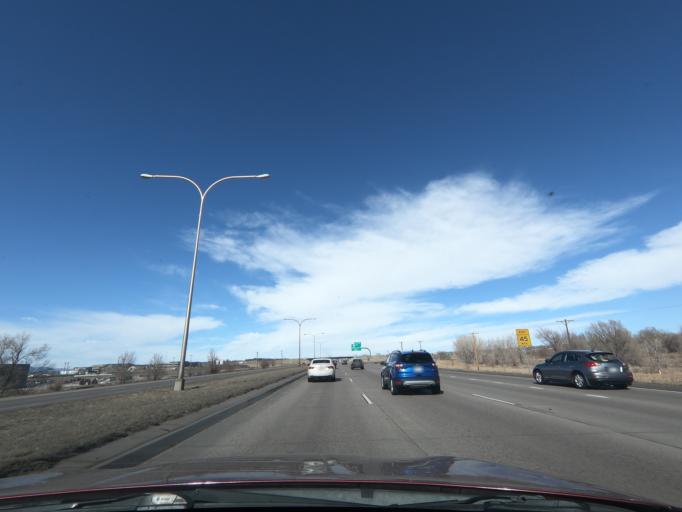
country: US
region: Colorado
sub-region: El Paso County
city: Cimarron Hills
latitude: 38.8332
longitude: -104.7207
